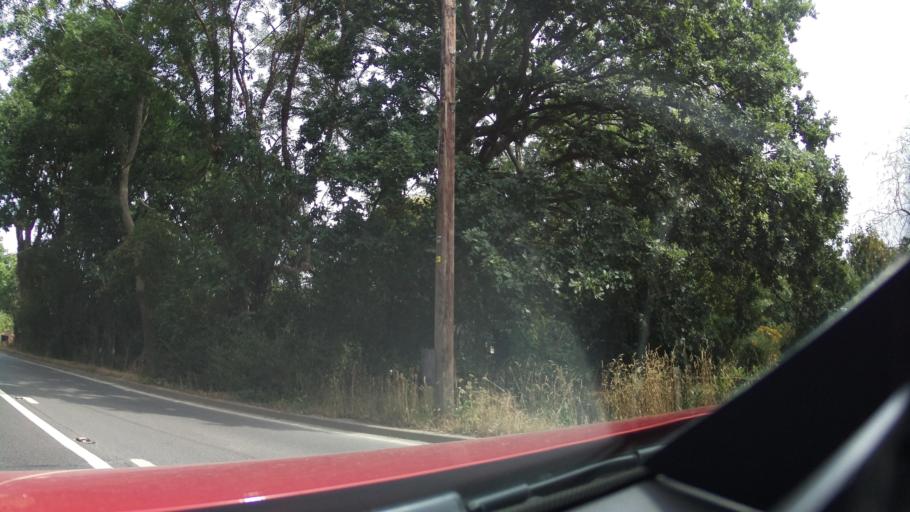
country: GB
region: England
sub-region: Surrey
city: Salfords
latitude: 51.1829
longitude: -0.1956
